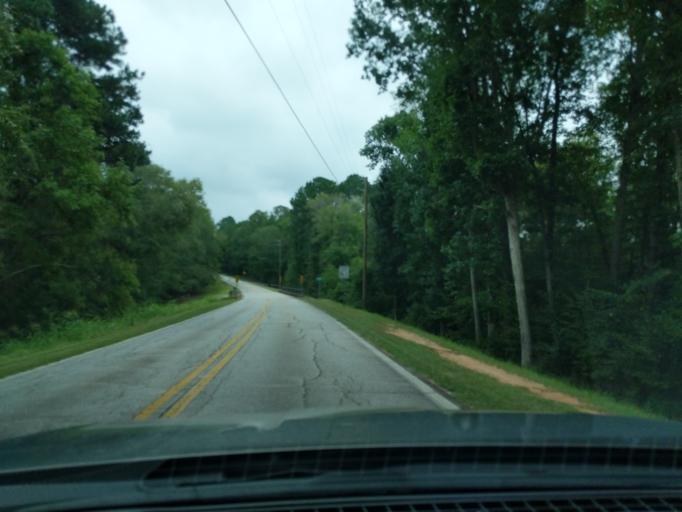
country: US
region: Georgia
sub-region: Columbia County
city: Appling
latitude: 33.5632
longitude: -82.3450
